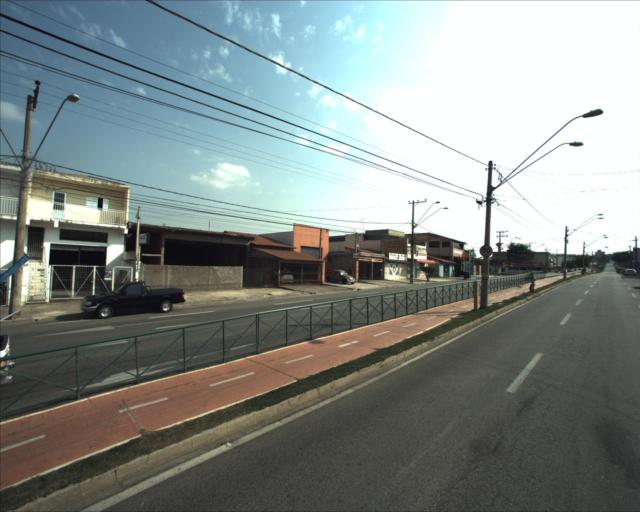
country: BR
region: Sao Paulo
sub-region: Sorocaba
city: Sorocaba
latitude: -23.4337
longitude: -47.4604
